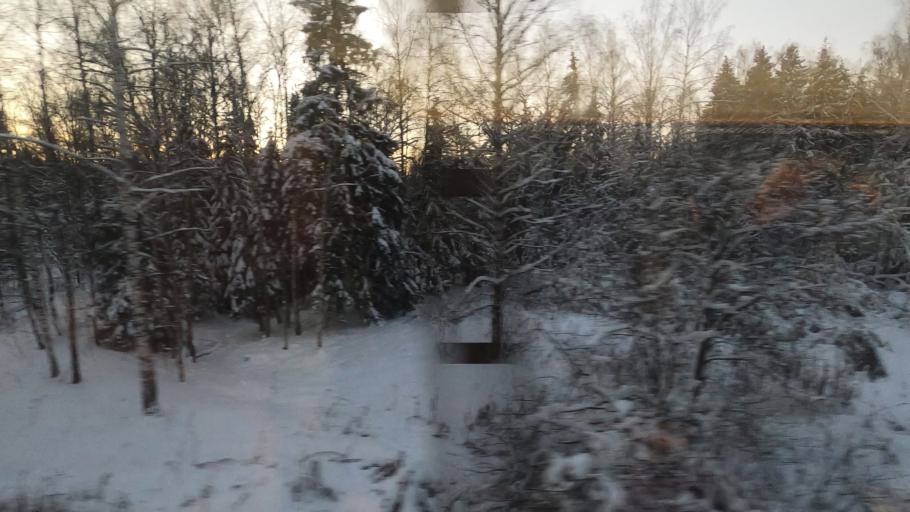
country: RU
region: Moskovskaya
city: Nekrasovskiy
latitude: 56.1096
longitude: 37.5140
